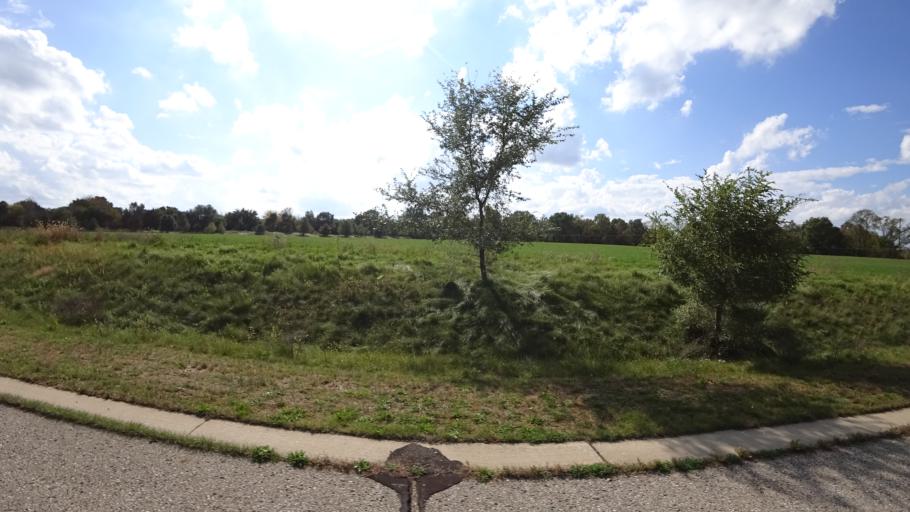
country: US
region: Michigan
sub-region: Saint Joseph County
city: Three Rivers
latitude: 41.9581
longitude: -85.6118
